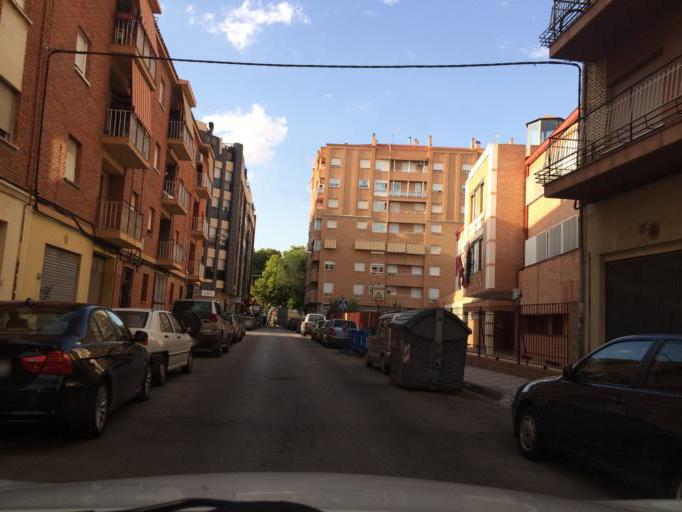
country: ES
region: Castille-La Mancha
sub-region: Provincia de Albacete
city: Albacete
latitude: 38.9953
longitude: -1.8659
